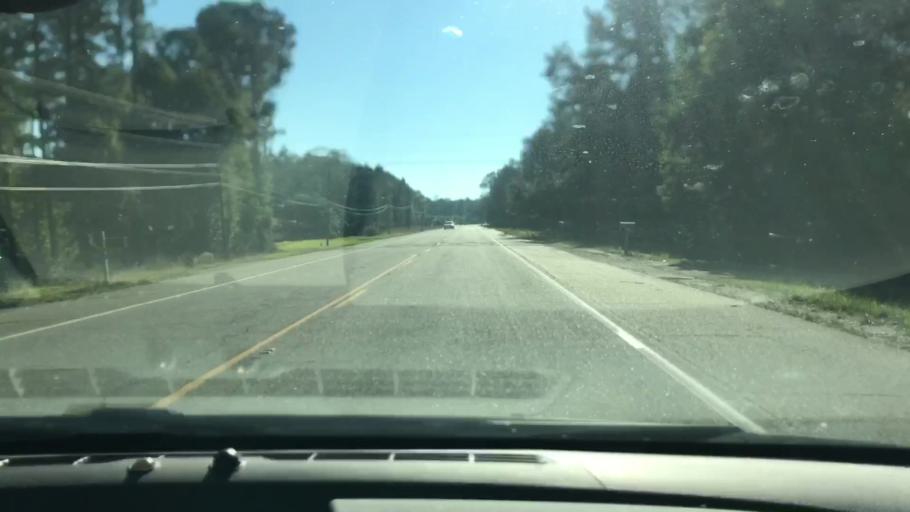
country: US
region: Louisiana
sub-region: Saint Tammany Parish
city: Pearl River
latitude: 30.4439
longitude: -89.7949
